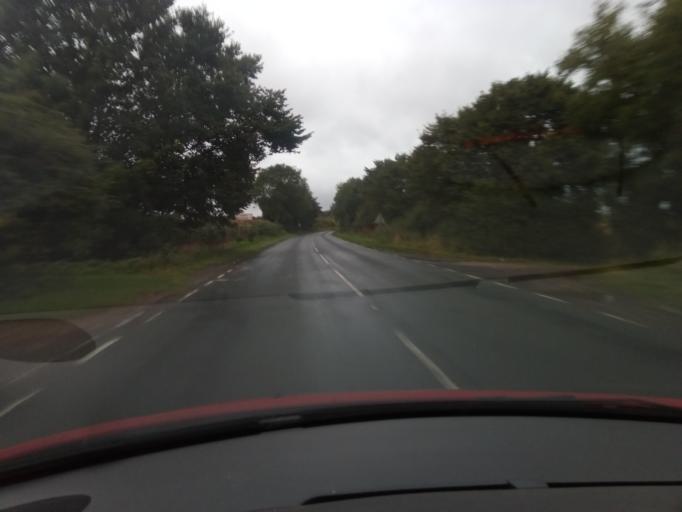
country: GB
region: England
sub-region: Darlington
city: High Coniscliffe
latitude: 54.4709
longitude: -1.6697
